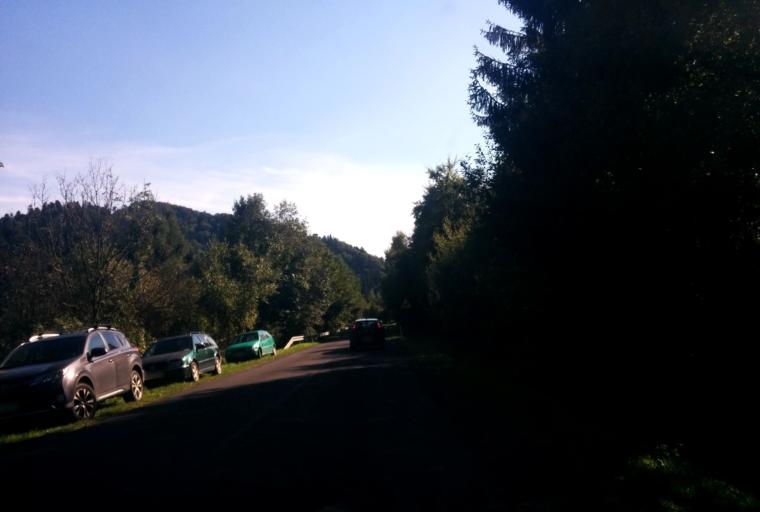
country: PL
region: Subcarpathian Voivodeship
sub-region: Powiat leski
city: Polanczyk
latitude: 49.3239
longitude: 22.4156
